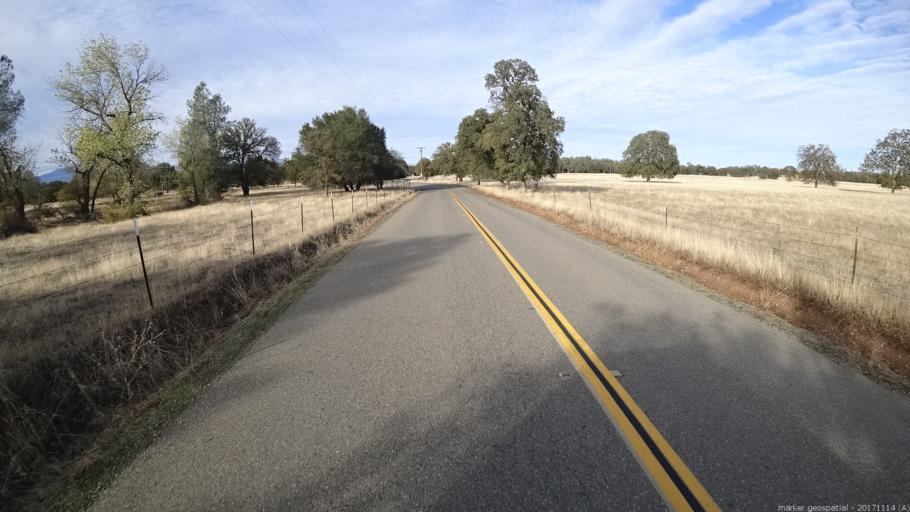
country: US
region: California
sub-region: Shasta County
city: Shasta
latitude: 40.3979
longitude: -122.5108
